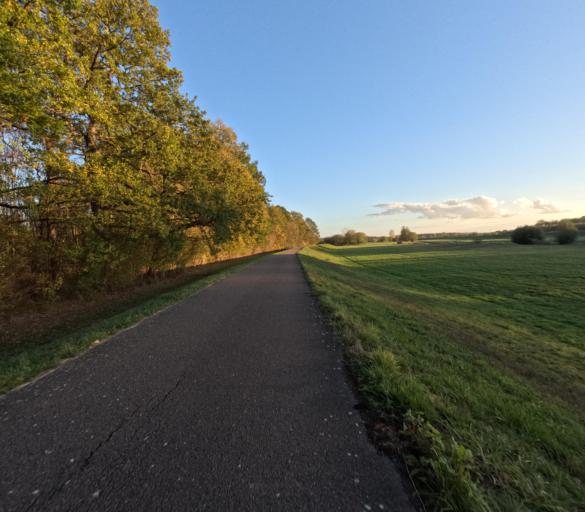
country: DE
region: Saxony-Anhalt
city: Ermlitz
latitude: 51.3846
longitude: 12.1777
